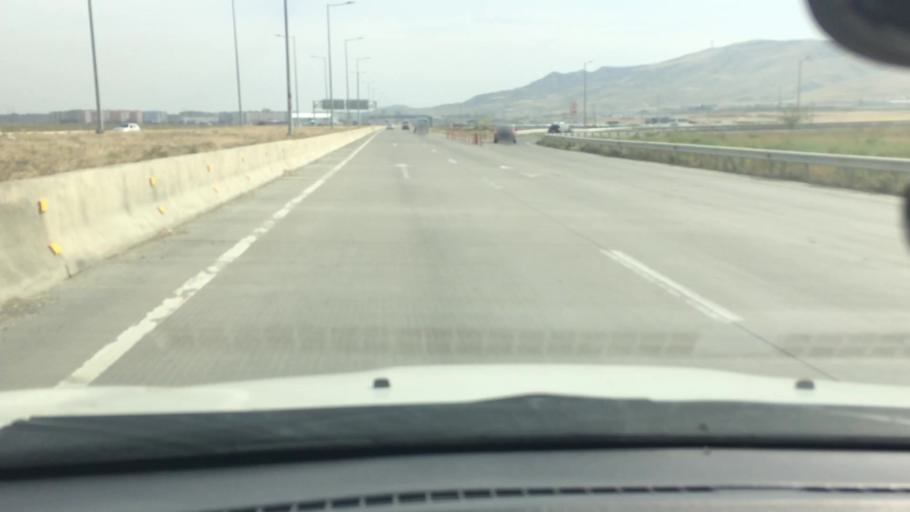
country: GE
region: Kvemo Kartli
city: Rust'avi
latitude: 41.5869
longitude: 44.9493
